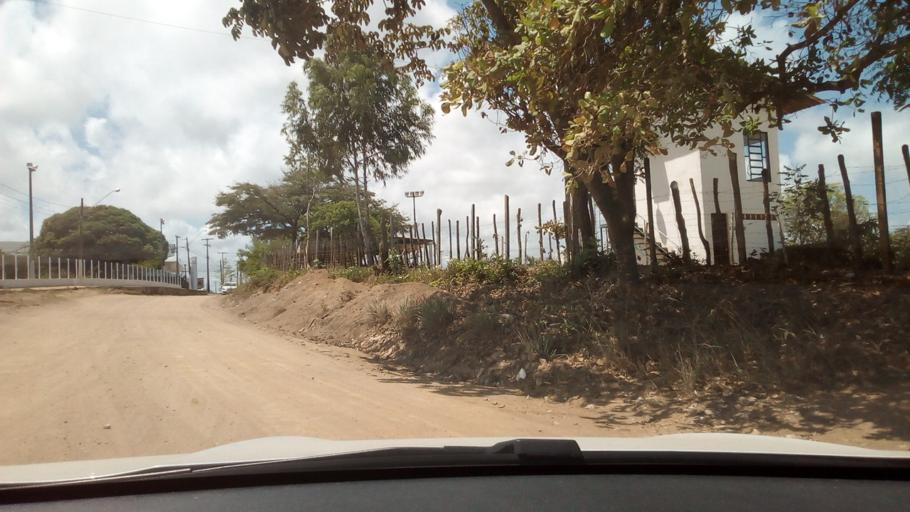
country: BR
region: Paraiba
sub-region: Joao Pessoa
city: Joao Pessoa
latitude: -7.1620
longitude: -34.8176
